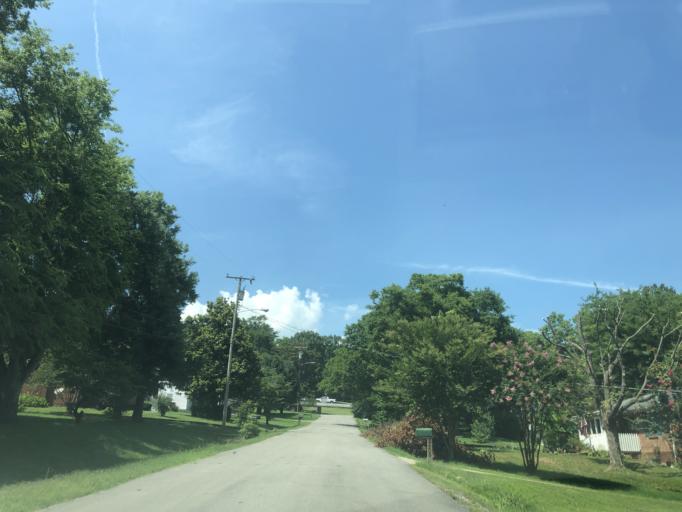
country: US
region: Tennessee
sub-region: Davidson County
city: Lakewood
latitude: 36.1715
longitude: -86.6681
